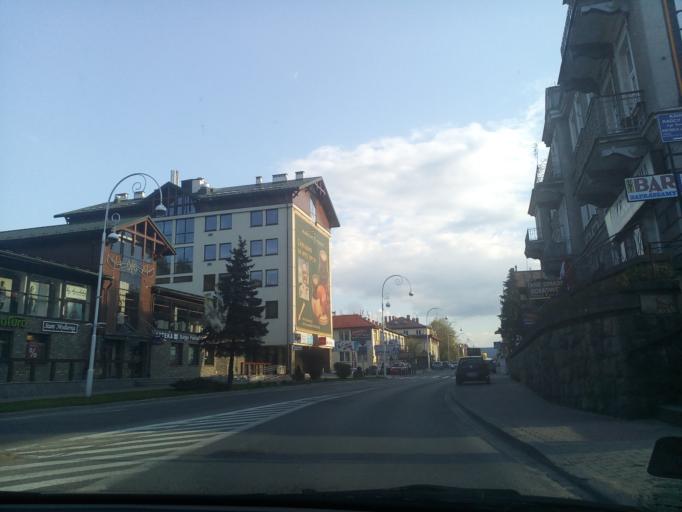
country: PL
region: Lesser Poland Voivodeship
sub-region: Powiat nowosadecki
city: Krynica-Zdroj
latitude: 49.4148
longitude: 20.9561
